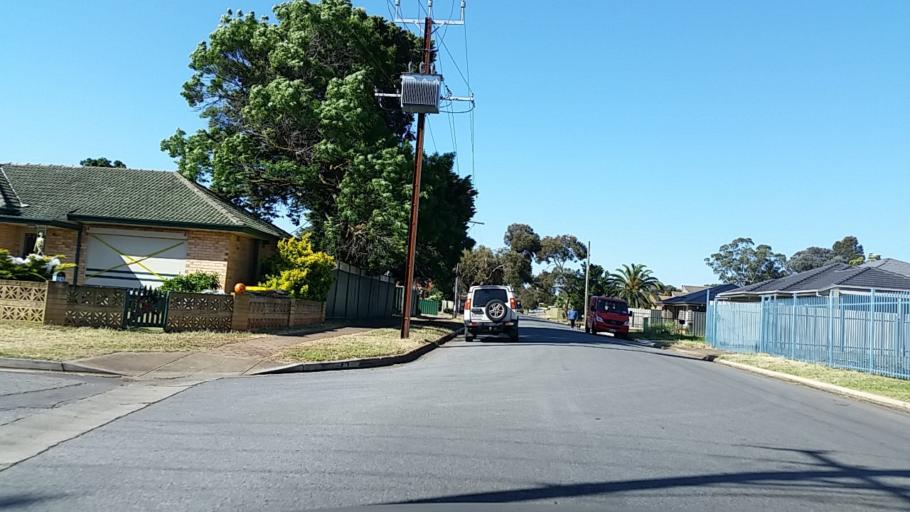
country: AU
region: South Australia
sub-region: Salisbury
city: Salisbury
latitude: -34.7812
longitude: 138.6540
